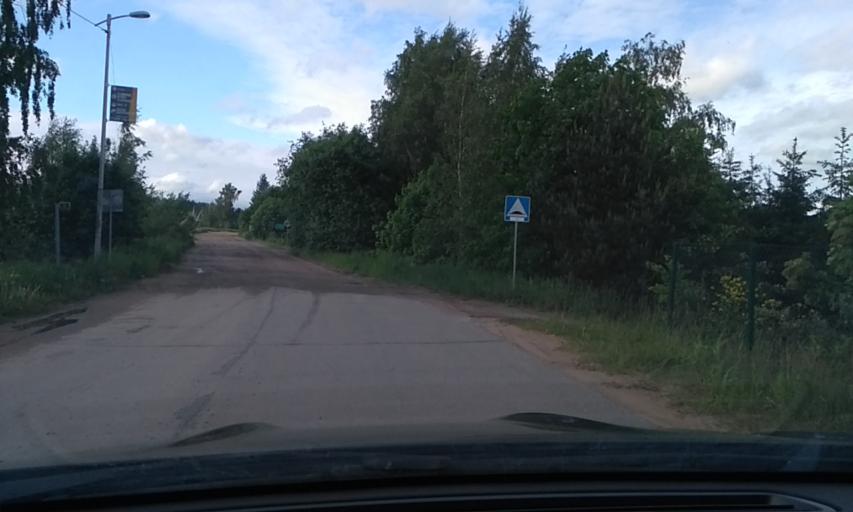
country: RU
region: Leningrad
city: Otradnoye
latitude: 59.7952
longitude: 30.7981
